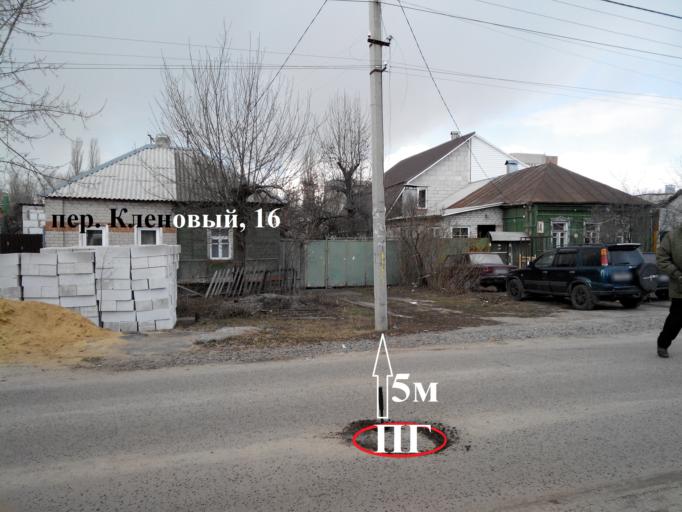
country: RU
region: Voronezj
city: Voronezh
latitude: 51.6377
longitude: 39.1624
